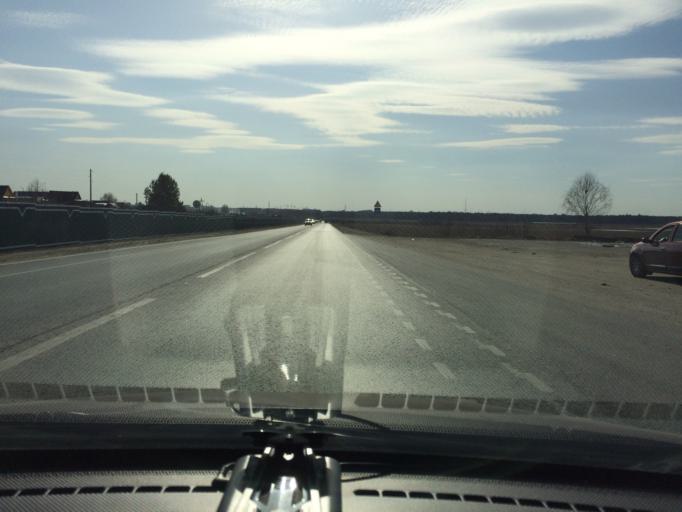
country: RU
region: Mariy-El
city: Yoshkar-Ola
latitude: 56.6591
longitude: 47.9708
